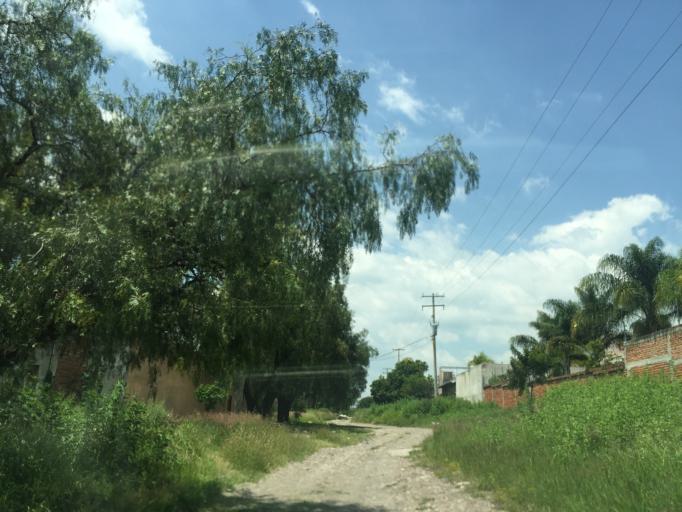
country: MX
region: Guanajuato
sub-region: Leon
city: La Ermita
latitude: 21.1582
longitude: -101.7212
